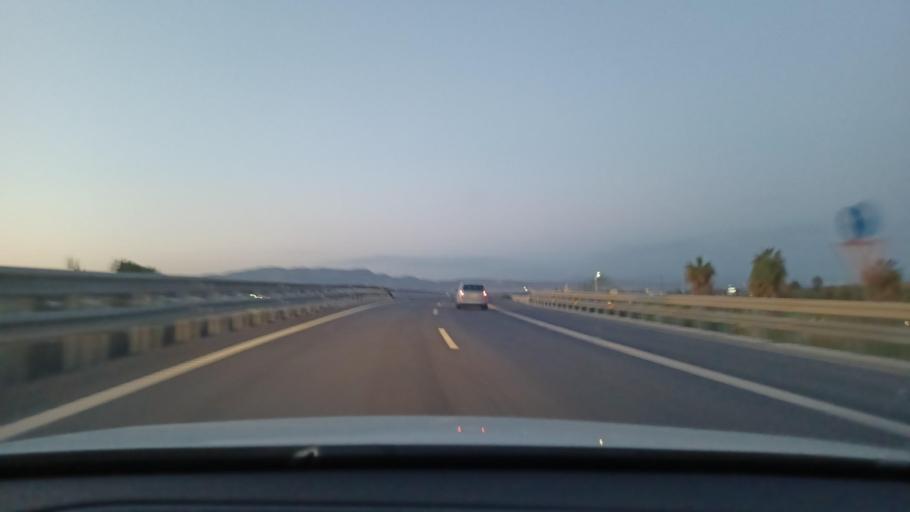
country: ES
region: Valencia
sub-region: Provincia de Alicante
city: Catral
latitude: 38.1504
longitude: -0.8200
